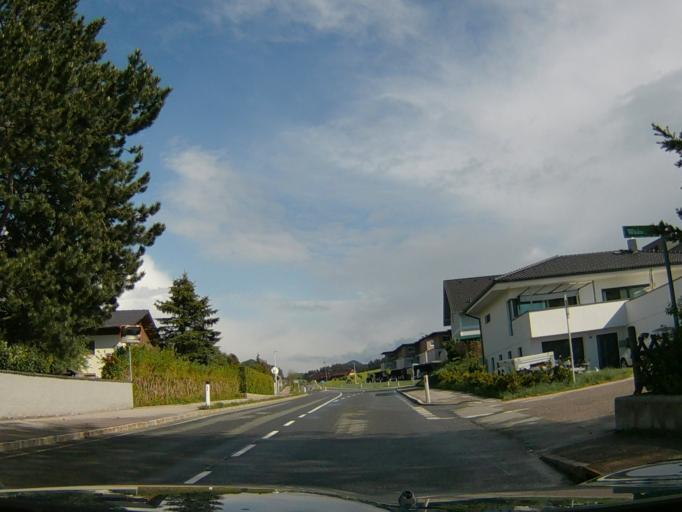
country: AT
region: Salzburg
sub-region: Politischer Bezirk Salzburg-Umgebung
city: Plainfeld
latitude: 47.8583
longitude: 13.1738
